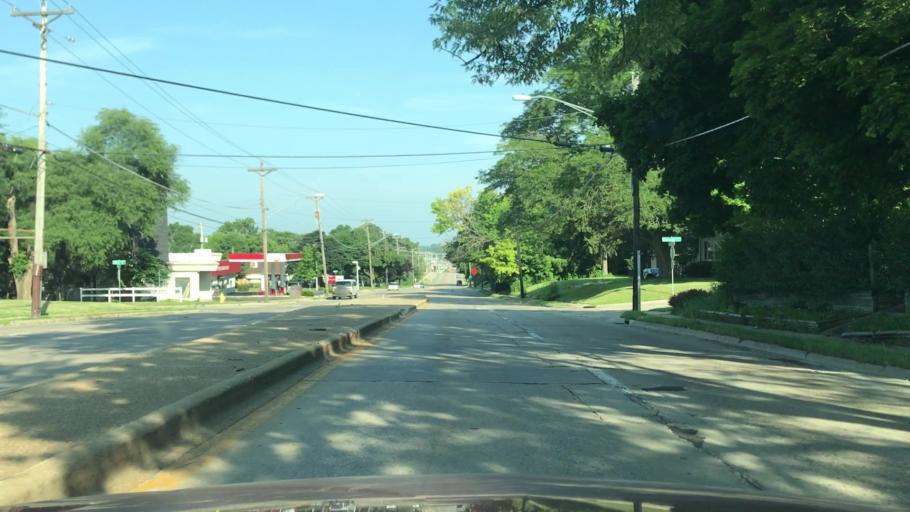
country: US
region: Illinois
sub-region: Winnebago County
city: Rockford
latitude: 42.2566
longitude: -89.0437
